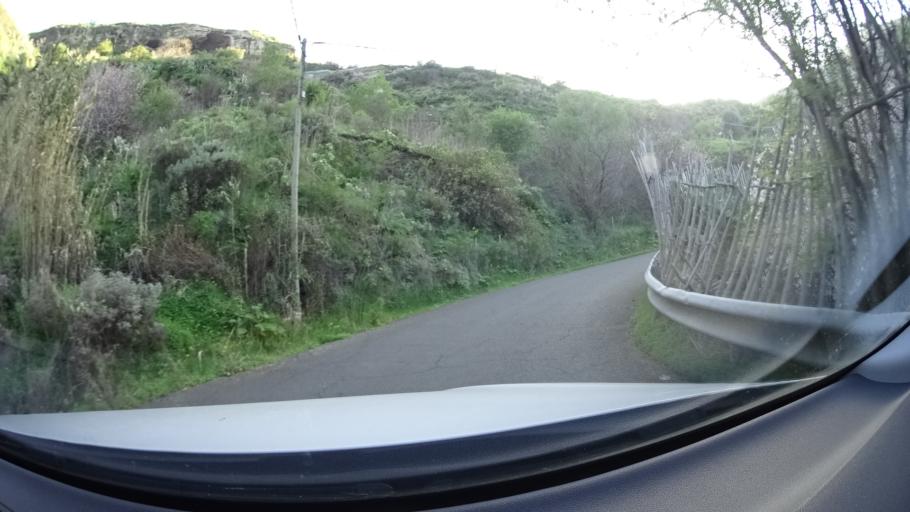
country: ES
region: Canary Islands
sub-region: Provincia de Las Palmas
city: Artenara
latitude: 28.0468
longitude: -15.6700
